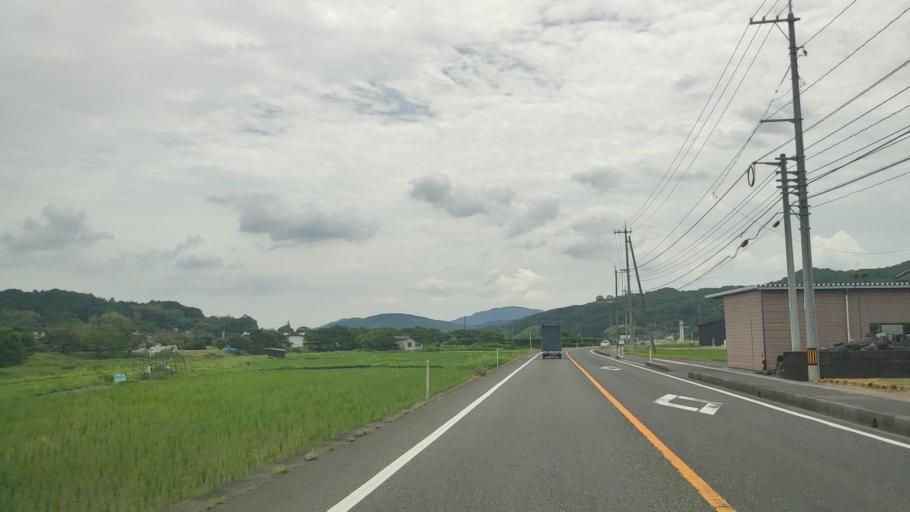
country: JP
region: Okayama
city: Tsuyama
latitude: 35.0573
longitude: 133.9065
